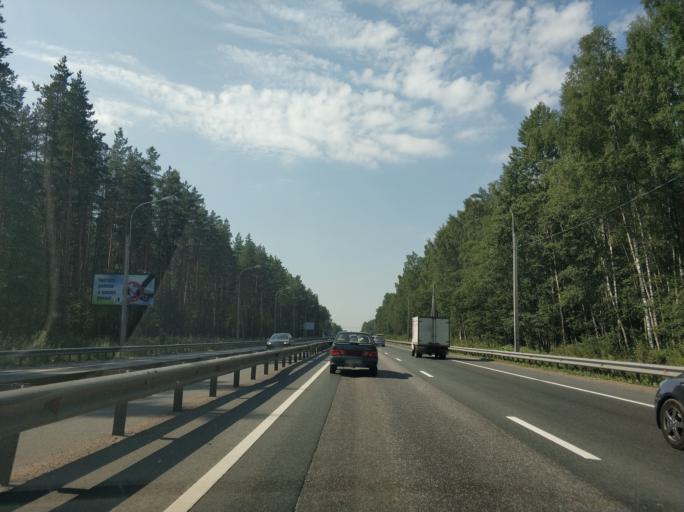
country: RU
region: St.-Petersburg
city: Krasnogvargeisky
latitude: 59.9992
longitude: 30.5505
